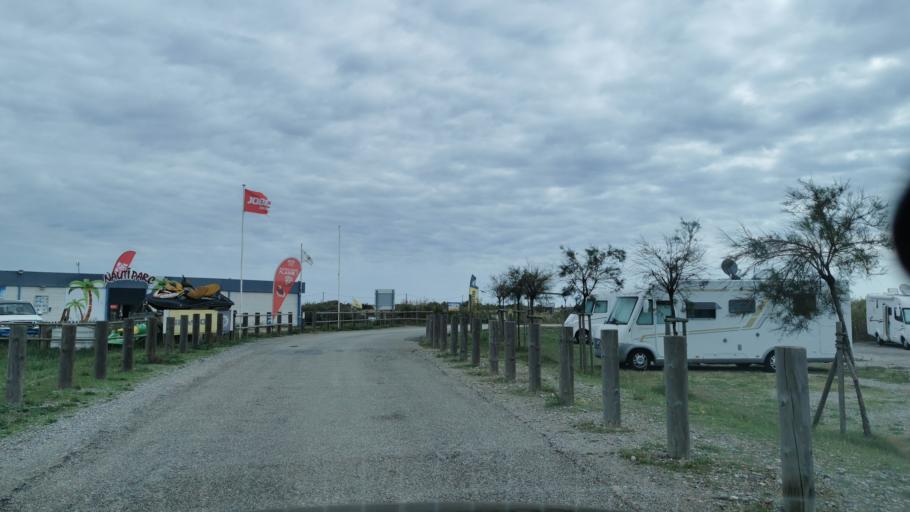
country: FR
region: Languedoc-Roussillon
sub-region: Departement de l'Herault
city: Vendres
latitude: 43.2154
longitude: 3.2343
